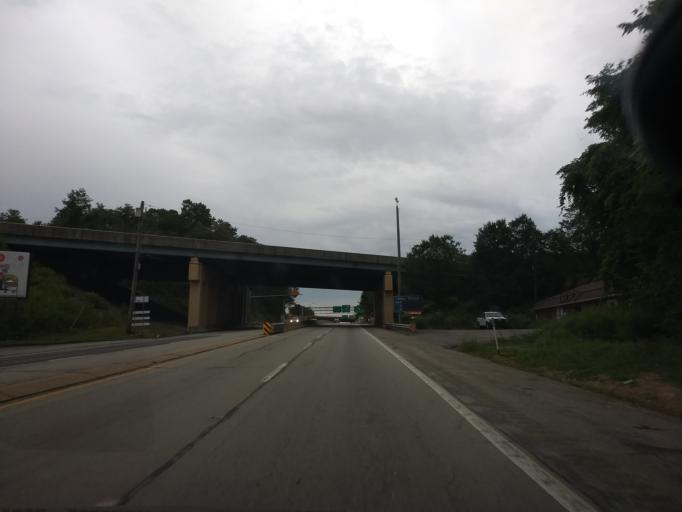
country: US
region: Pennsylvania
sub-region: Allegheny County
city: Monroeville
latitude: 40.4388
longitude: -79.7499
